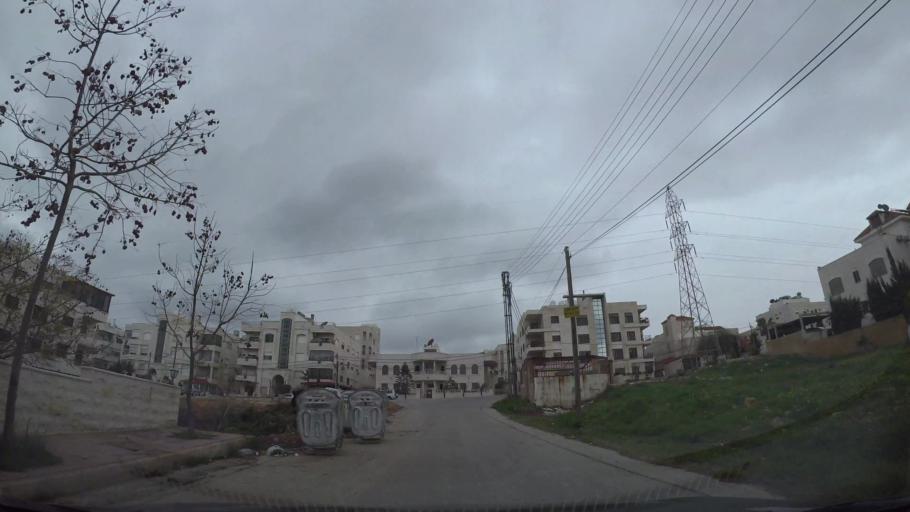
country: JO
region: Amman
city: Wadi as Sir
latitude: 31.9642
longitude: 35.8257
